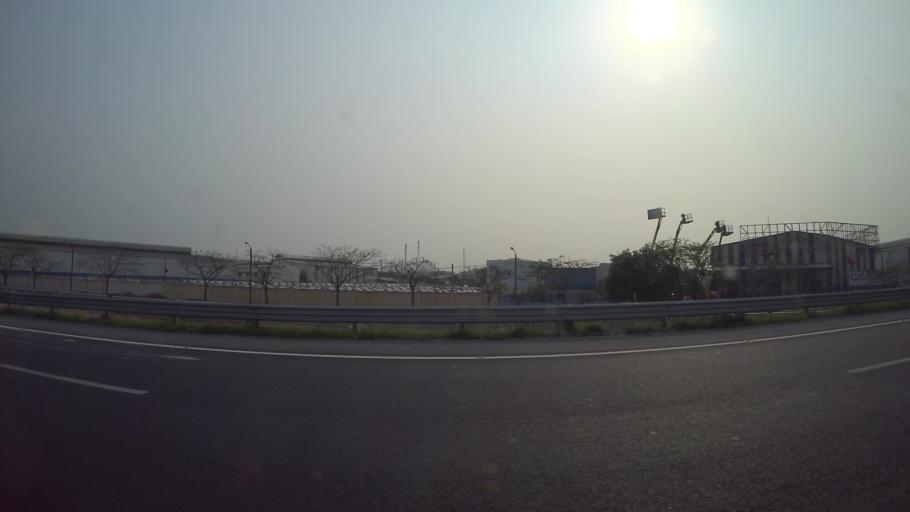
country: VN
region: Ha Noi
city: Thuong Tin
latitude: 20.8790
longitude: 105.8738
